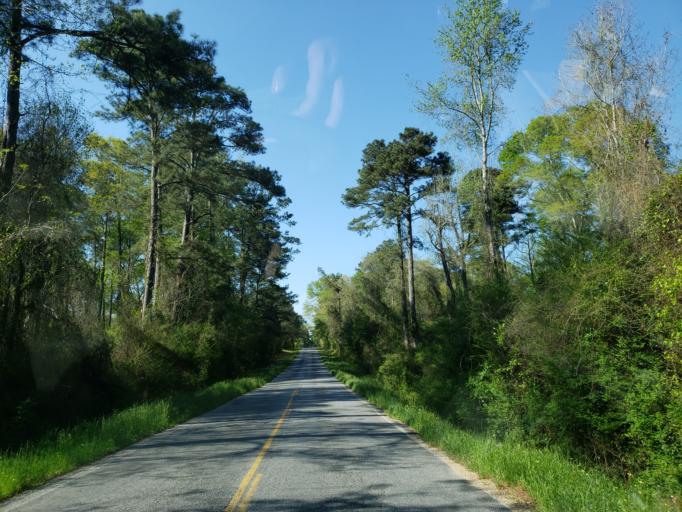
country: US
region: Mississippi
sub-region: Forrest County
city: Rawls Springs
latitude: 31.5237
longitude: -89.3589
